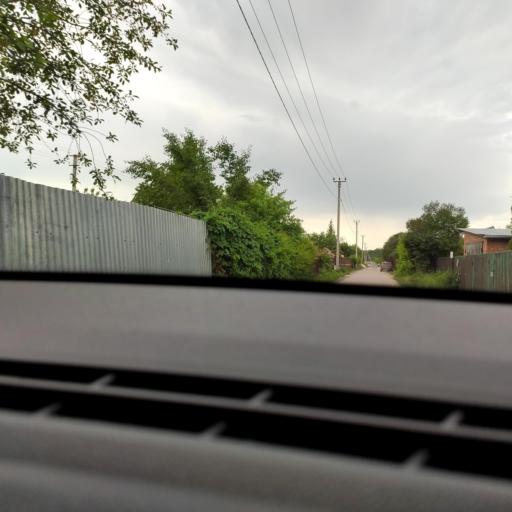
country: RU
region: Samara
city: Podstepki
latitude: 53.5120
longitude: 49.0737
